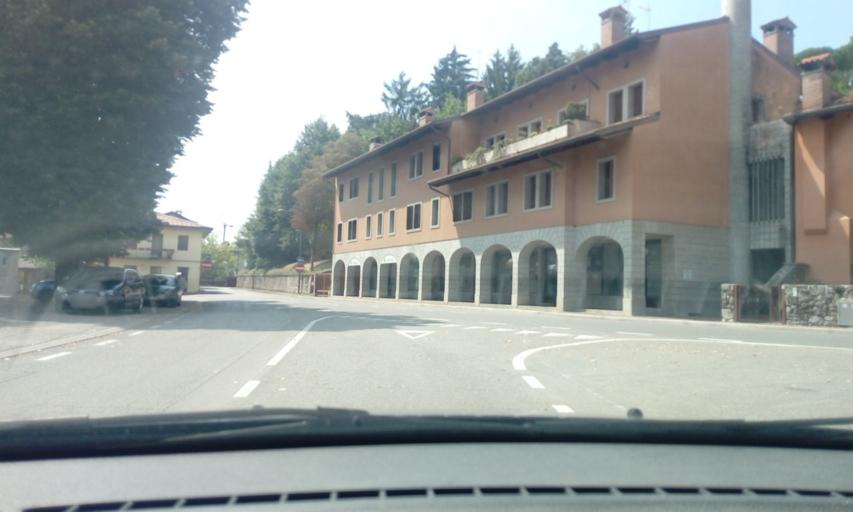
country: IT
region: Friuli Venezia Giulia
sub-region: Provincia di Udine
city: Tricesimo
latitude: 46.1608
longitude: 13.2162
